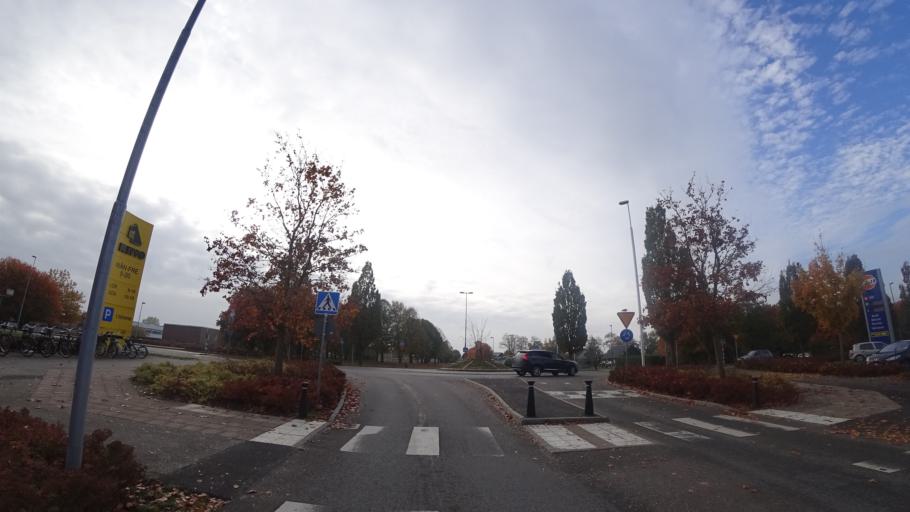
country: SE
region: Skane
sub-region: Staffanstorps Kommun
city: Staffanstorp
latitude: 55.6407
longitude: 13.1952
